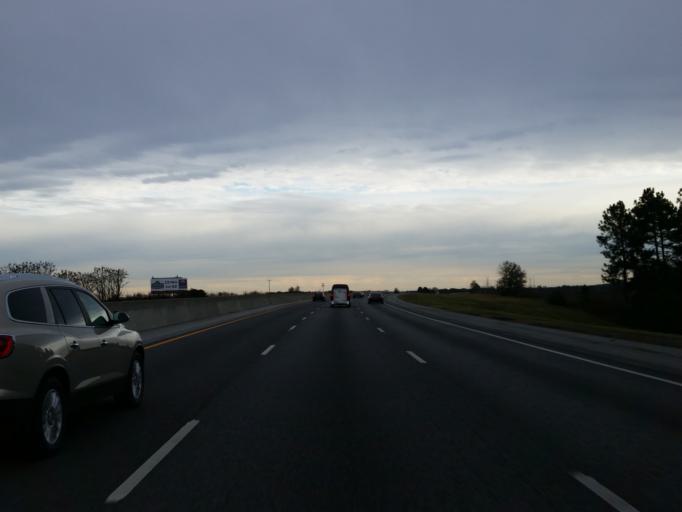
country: US
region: Georgia
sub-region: Turner County
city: Ashburn
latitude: 31.6178
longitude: -83.5695
